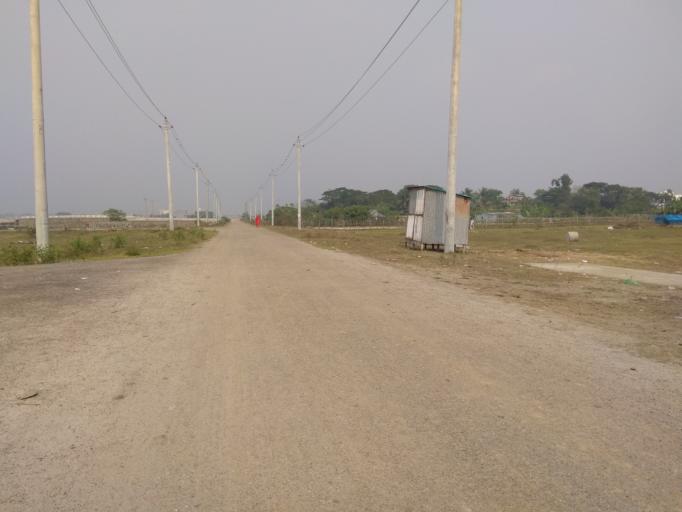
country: BD
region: Dhaka
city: Tungi
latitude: 23.8570
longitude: 90.3724
